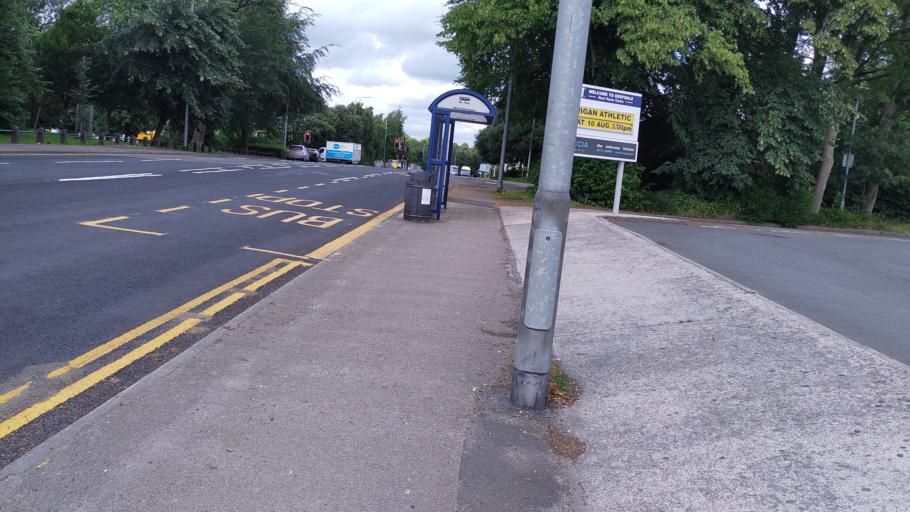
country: GB
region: England
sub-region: Lancashire
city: Preston
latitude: 53.7736
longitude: -2.6899
